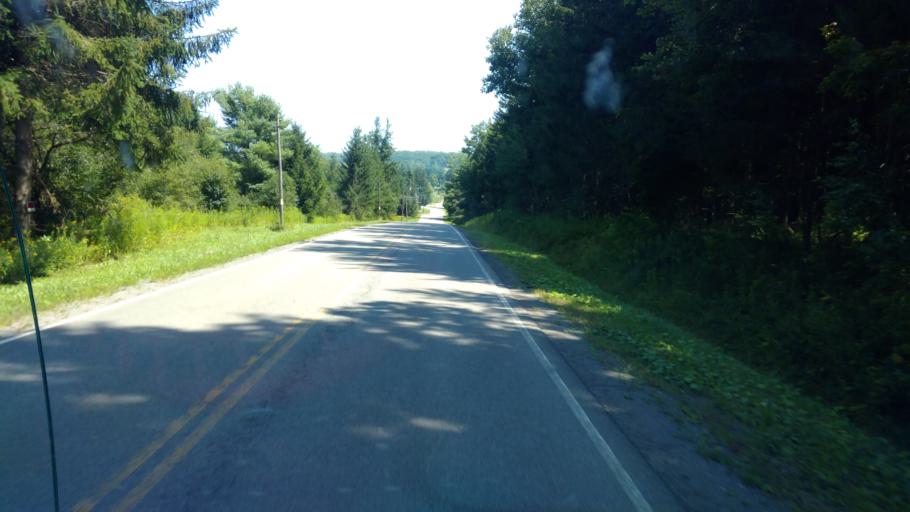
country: US
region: New York
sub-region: Allegany County
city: Alfred
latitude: 42.2987
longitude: -77.8891
